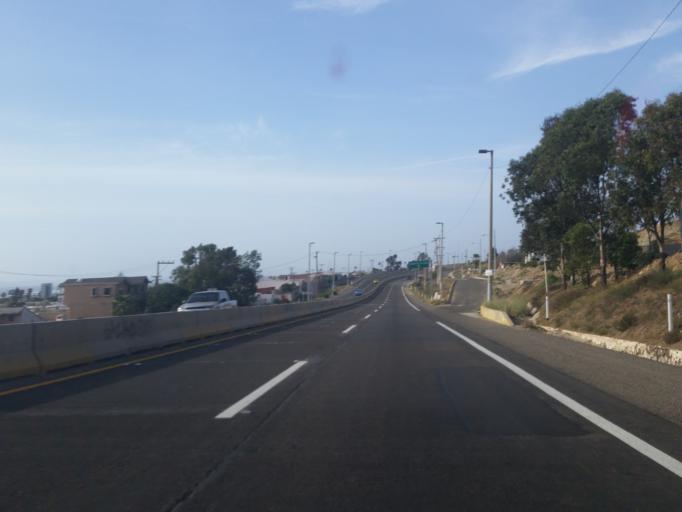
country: US
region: California
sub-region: San Diego County
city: Imperial Beach
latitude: 32.5288
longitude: -117.1081
